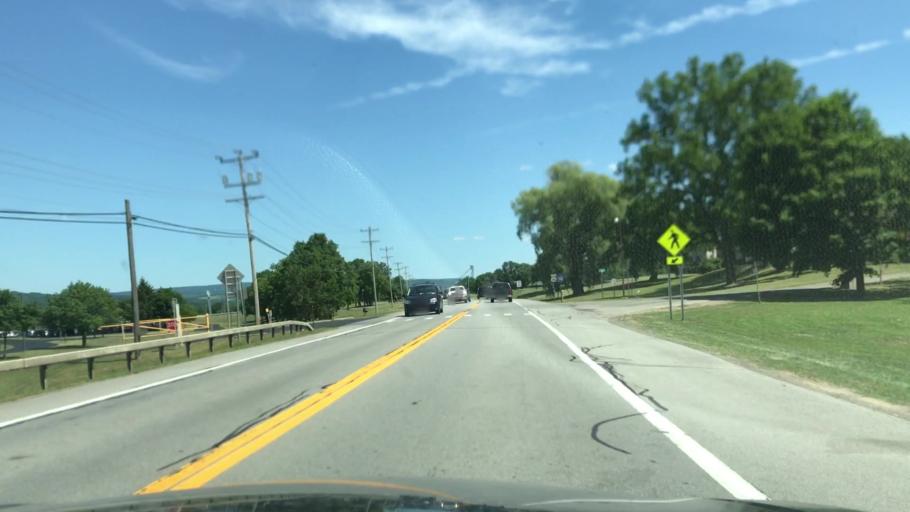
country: US
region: New York
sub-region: Livingston County
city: Mount Morris
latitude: 42.6828
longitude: -77.8276
